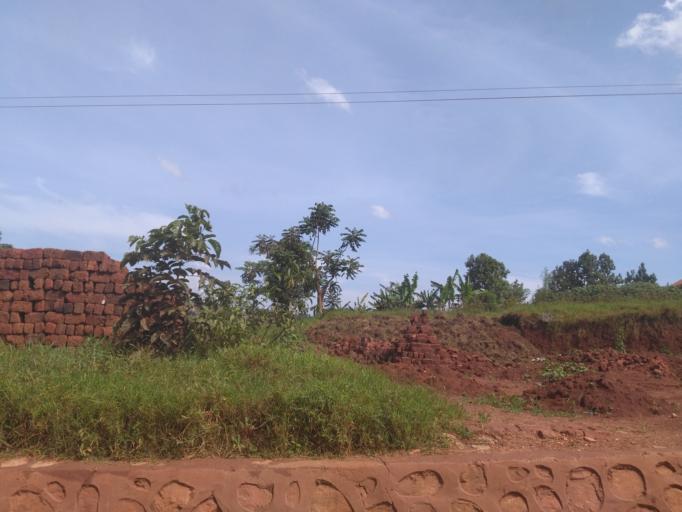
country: UG
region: Central Region
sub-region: Wakiso District
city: Kireka
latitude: 0.4408
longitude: 32.5961
